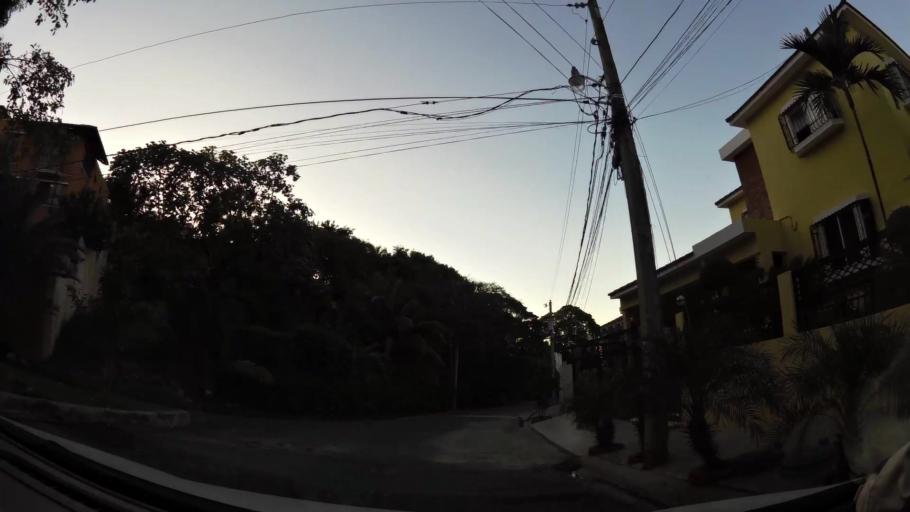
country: DO
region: Nacional
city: Santo Domingo
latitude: 18.4932
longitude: -69.9620
